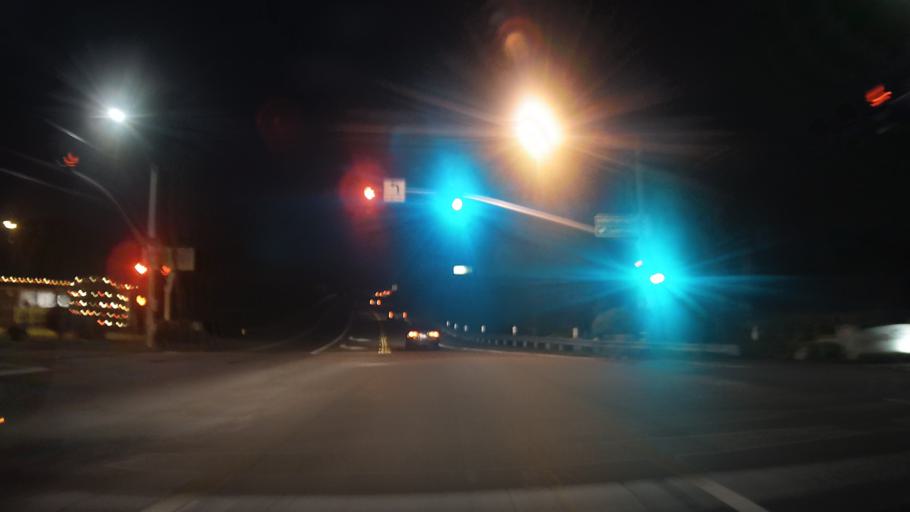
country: US
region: California
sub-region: San Diego County
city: Jamul
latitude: 32.7201
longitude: -116.8805
